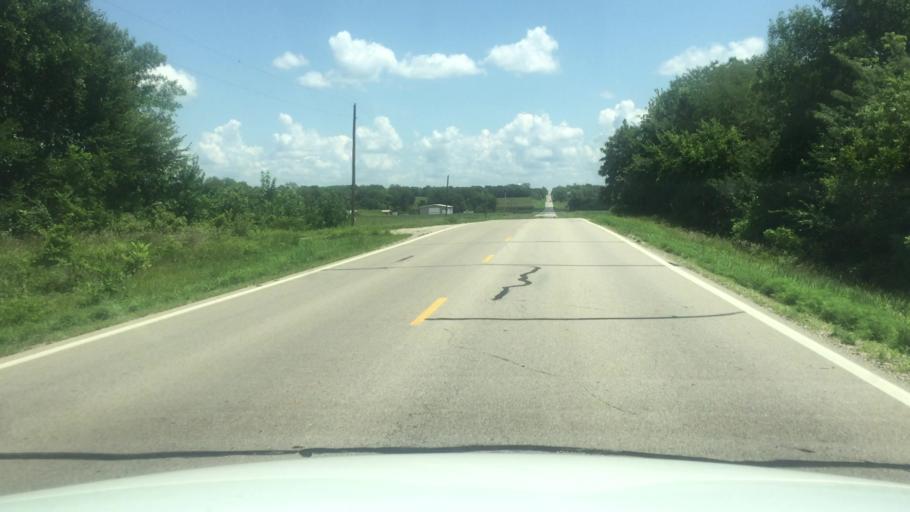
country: US
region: Kansas
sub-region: Brown County
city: Horton
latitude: 39.6673
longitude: -95.5547
